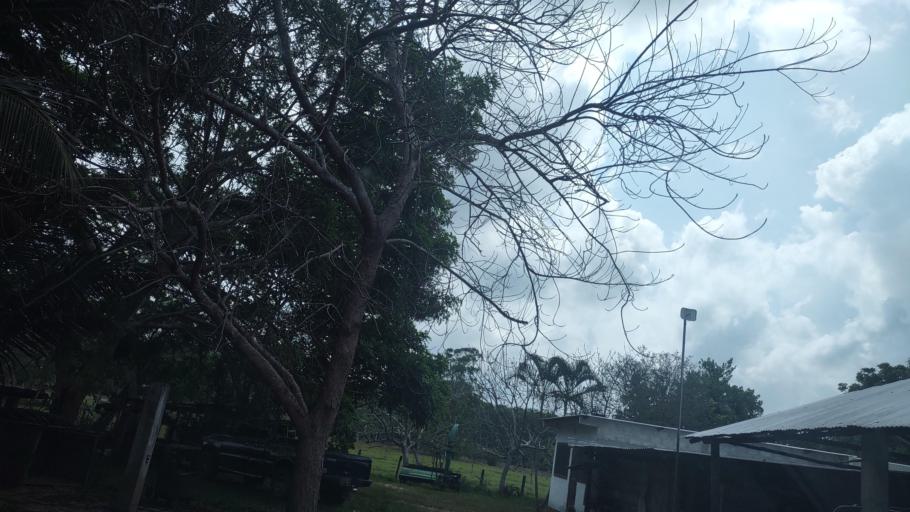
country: MX
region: Veracruz
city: Las Choapas
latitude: 17.9476
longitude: -94.1112
